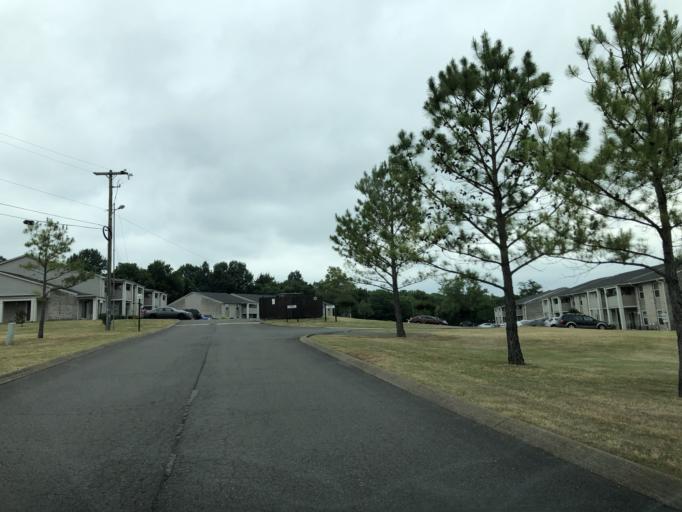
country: US
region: Tennessee
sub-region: Davidson County
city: Goodlettsville
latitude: 36.2892
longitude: -86.7200
